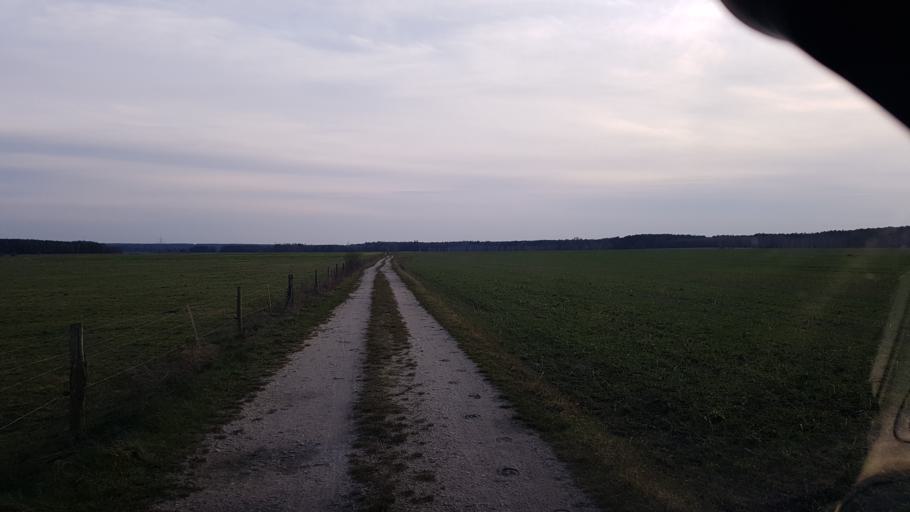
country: DE
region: Brandenburg
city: Schonborn
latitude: 51.5916
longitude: 13.5048
